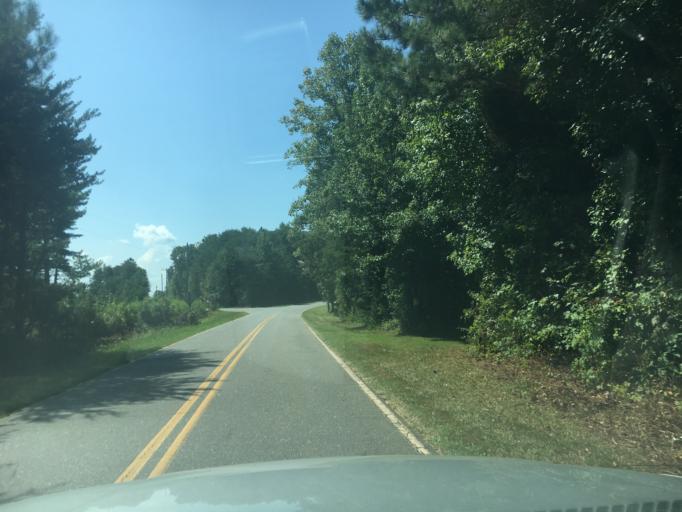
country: US
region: South Carolina
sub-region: Spartanburg County
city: Boiling Springs
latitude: 35.1981
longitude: -82.0309
